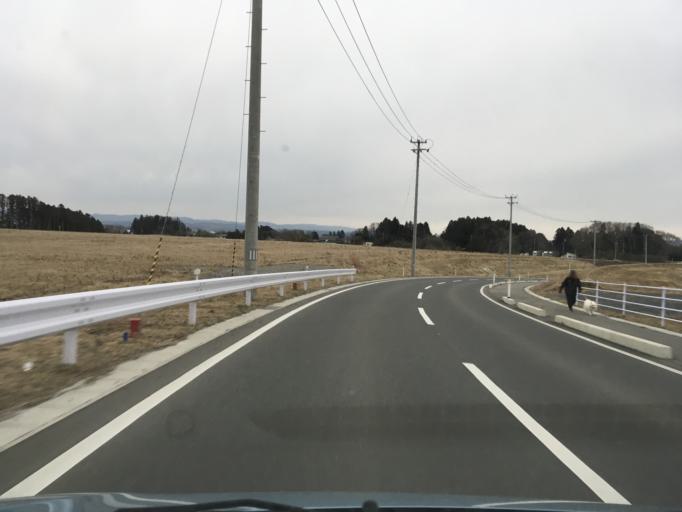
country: JP
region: Miyagi
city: Wakuya
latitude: 38.6957
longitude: 141.1707
